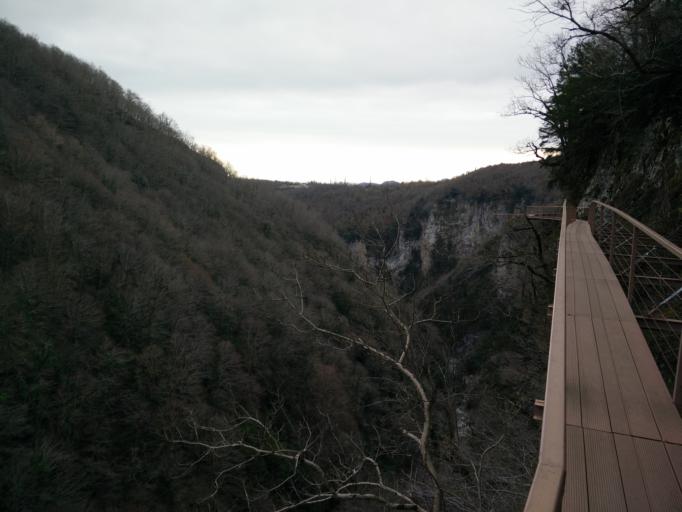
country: GE
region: Imereti
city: Tsqaltubo
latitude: 42.4527
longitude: 42.5503
